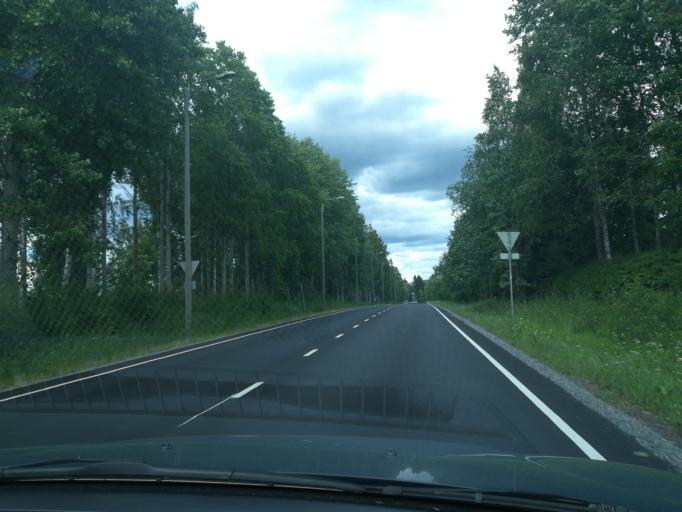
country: FI
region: Southern Savonia
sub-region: Mikkeli
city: Mikkeli
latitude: 61.6451
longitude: 27.0806
